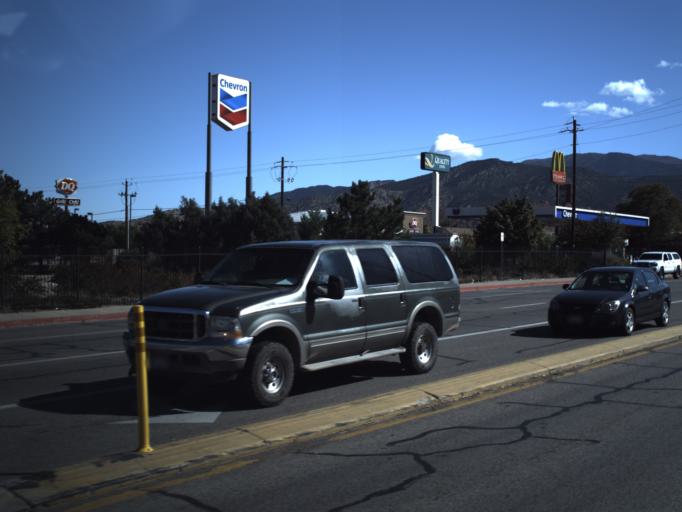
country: US
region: Utah
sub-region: Iron County
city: Cedar City
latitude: 37.6808
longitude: -113.0788
